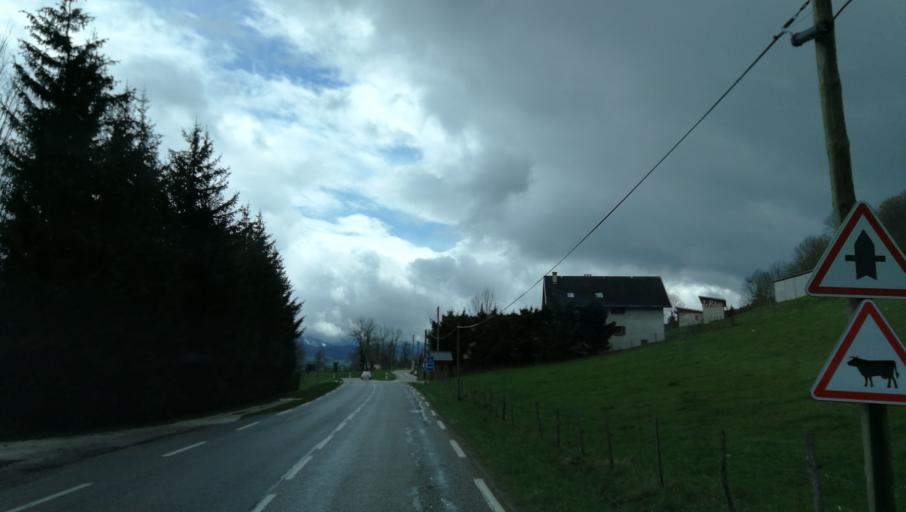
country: FR
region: Rhone-Alpes
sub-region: Departement de l'Isere
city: Lans-en-Vercors
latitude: 45.1188
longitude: 5.5722
